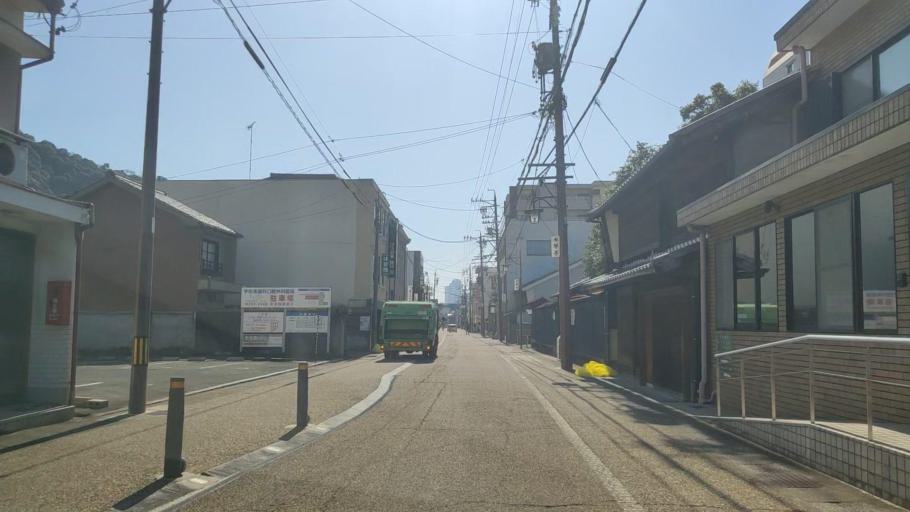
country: JP
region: Gifu
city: Gifu-shi
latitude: 35.4303
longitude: 136.7669
